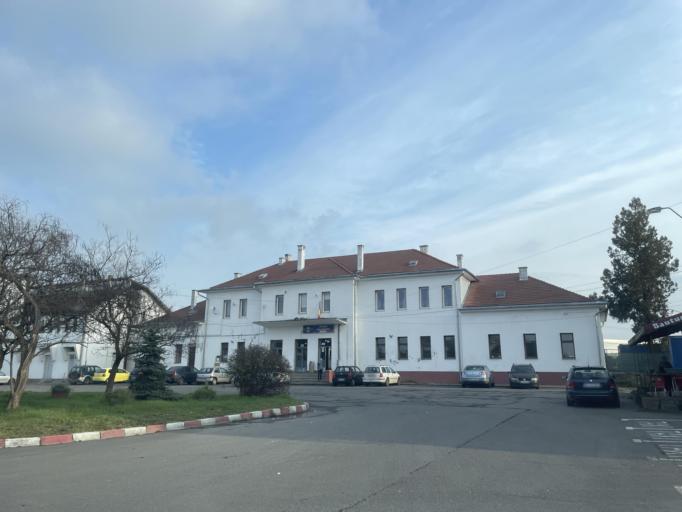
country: RO
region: Mures
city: Reghin-Sat
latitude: 46.7805
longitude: 24.7185
